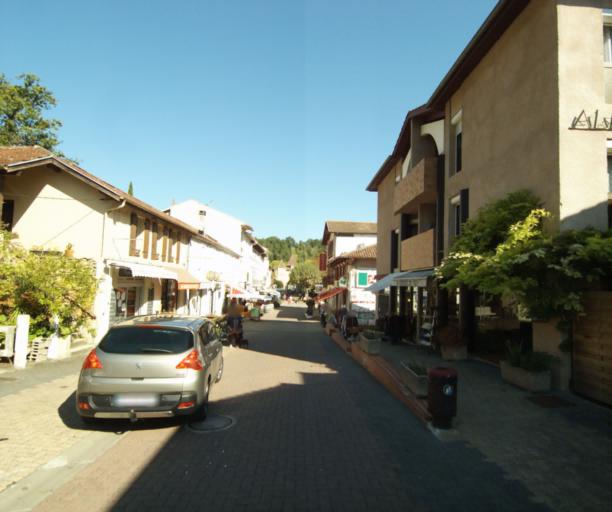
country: FR
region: Midi-Pyrenees
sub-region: Departement du Gers
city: Cazaubon
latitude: 43.9497
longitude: -0.0443
